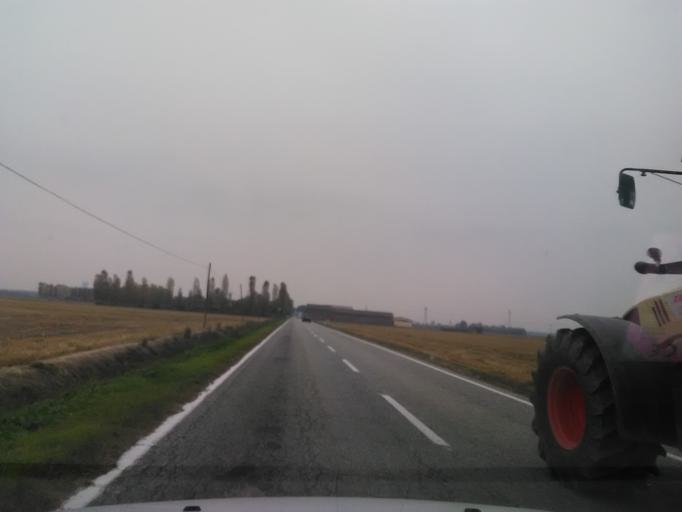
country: IT
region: Piedmont
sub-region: Provincia di Vercelli
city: Fontanetto Po
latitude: 45.2479
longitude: 8.1740
